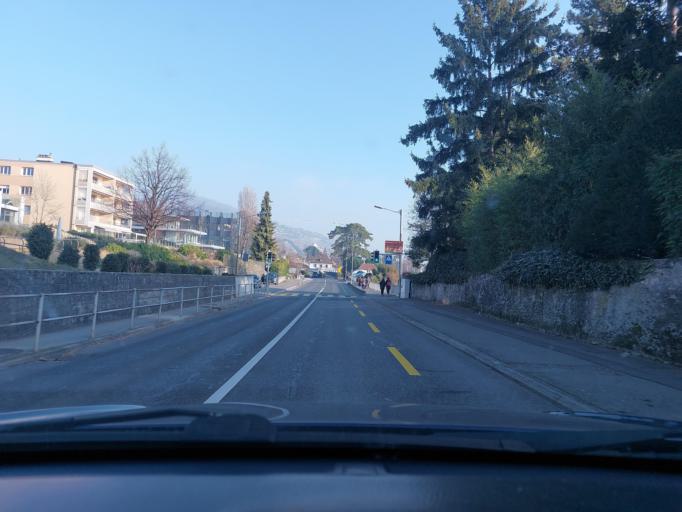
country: CH
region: Vaud
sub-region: Lavaux-Oron District
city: Paudex
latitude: 46.5044
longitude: 6.6762
